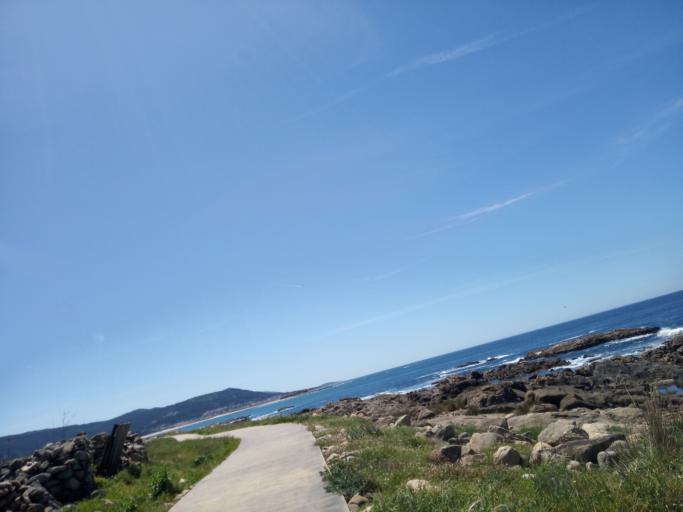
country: ES
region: Galicia
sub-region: Provincia de Pontevedra
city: A Guarda
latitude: 41.8757
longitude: -8.8765
